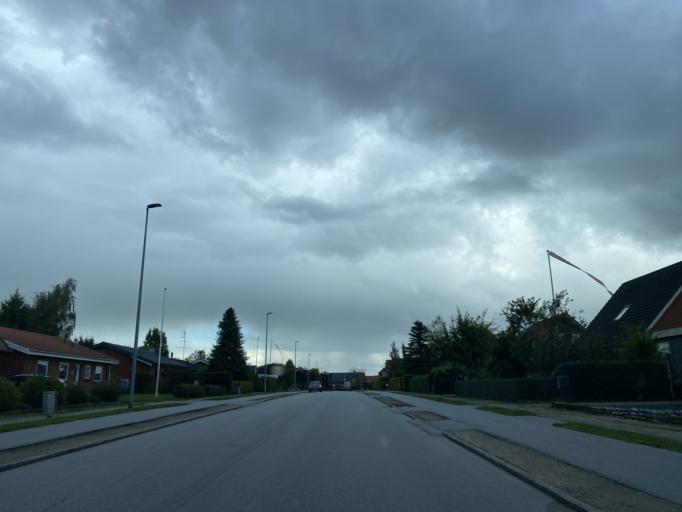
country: DK
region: South Denmark
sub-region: Haderslev Kommune
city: Haderslev
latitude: 55.2433
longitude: 9.4994
